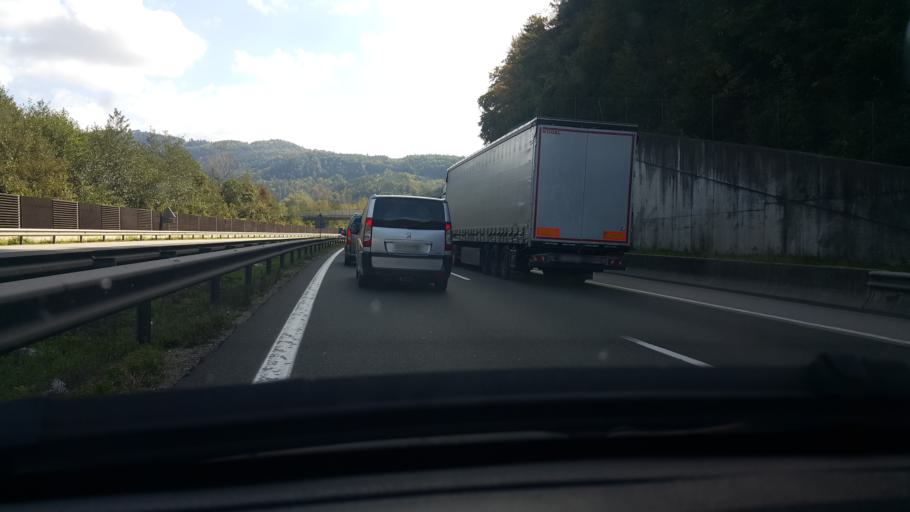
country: SI
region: Moravce
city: Moravce
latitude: 46.1691
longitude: 14.7363
